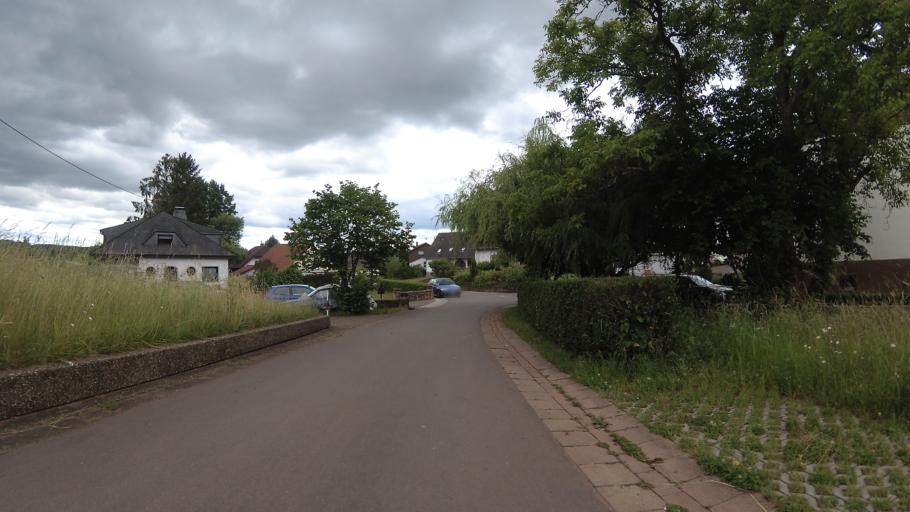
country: DE
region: Saarland
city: Nalbach
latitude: 49.3938
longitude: 6.8204
